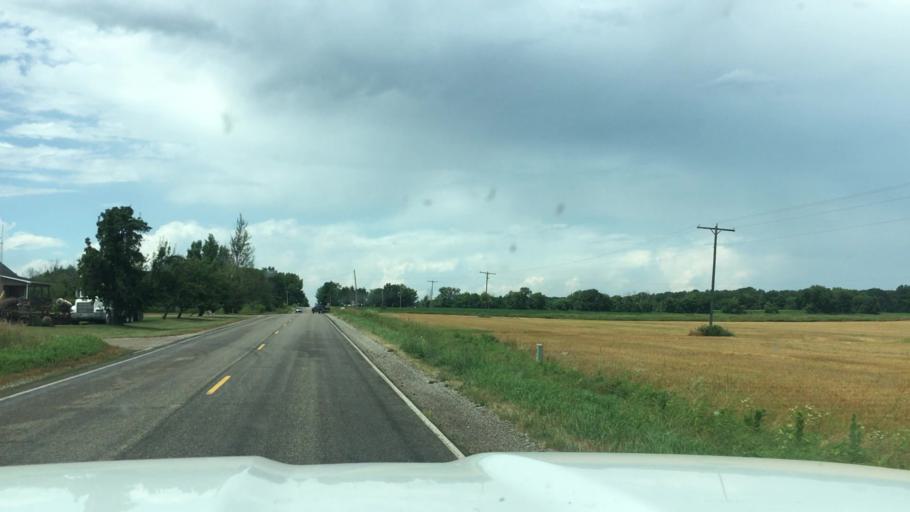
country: US
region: Michigan
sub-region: Montcalm County
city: Carson City
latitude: 43.2323
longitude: -84.7775
